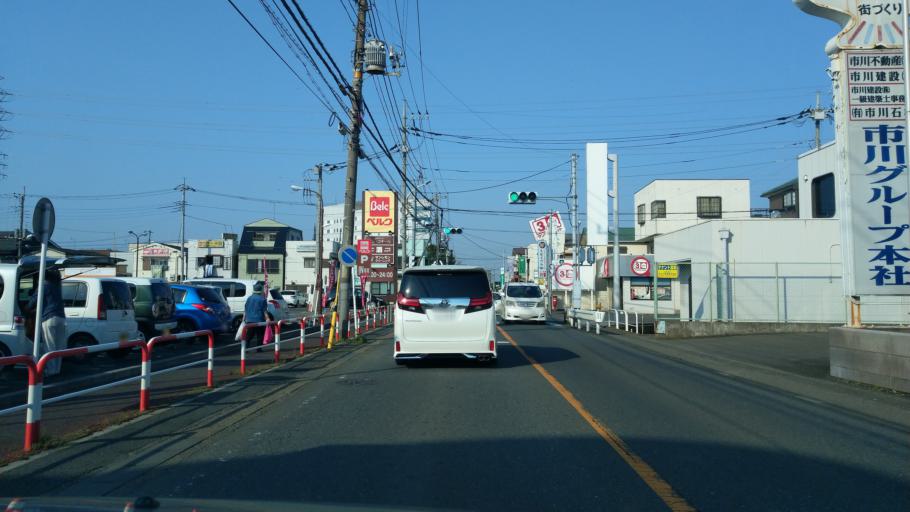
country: JP
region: Saitama
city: Kamifukuoka
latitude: 35.8595
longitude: 139.5012
